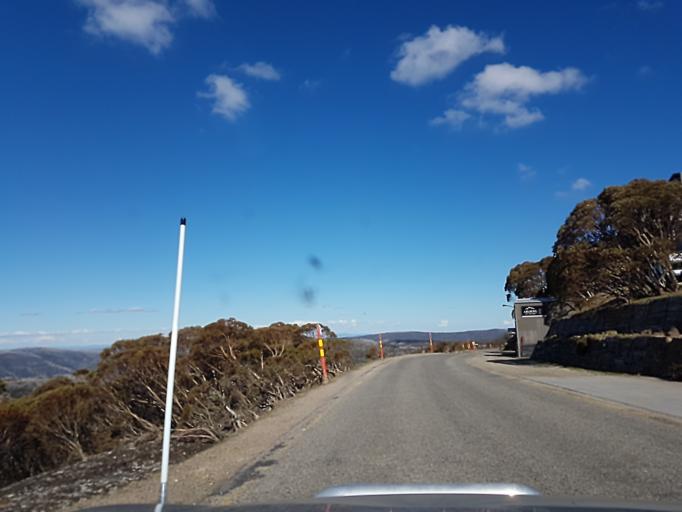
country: AU
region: Victoria
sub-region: Alpine
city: Mount Beauty
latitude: -36.9838
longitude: 147.1445
